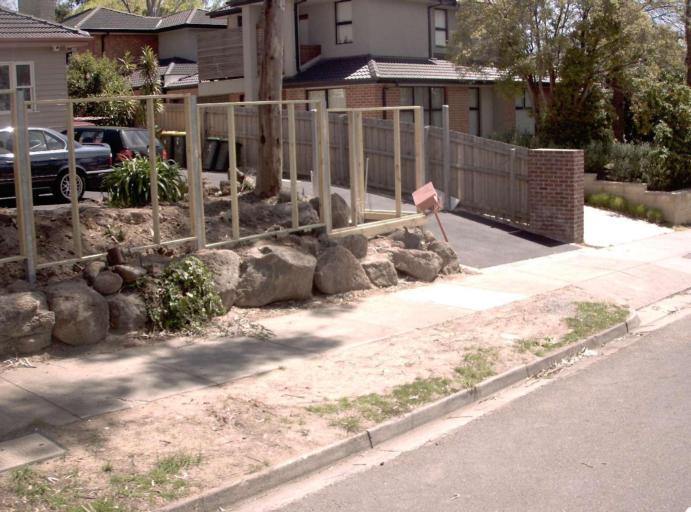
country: AU
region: Victoria
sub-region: Whitehorse
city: Blackburn South
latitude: -37.8362
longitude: 145.1561
